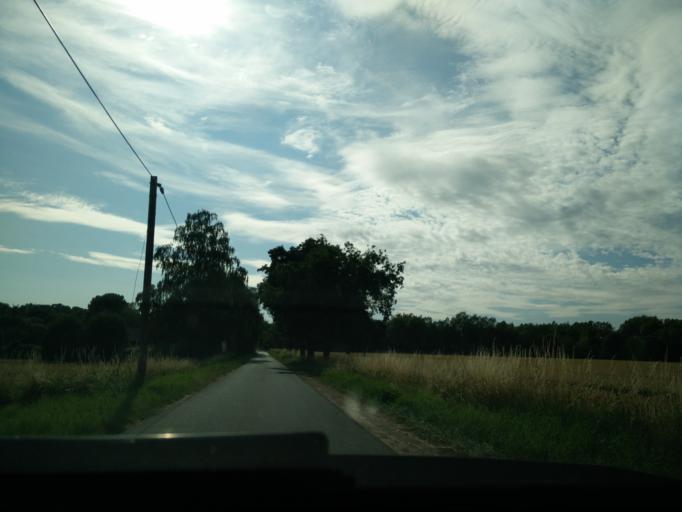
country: DE
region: Saxony
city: Geithain
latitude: 51.0719
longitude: 12.6937
